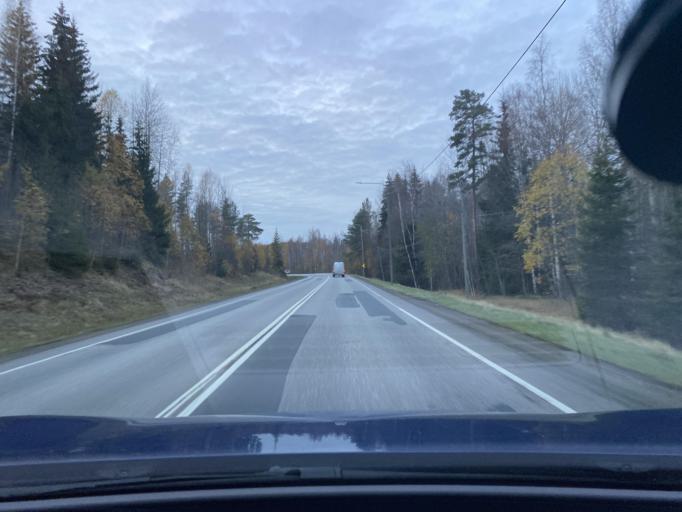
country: FI
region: Uusimaa
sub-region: Helsinki
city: Vihti
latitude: 60.3268
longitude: 24.2141
